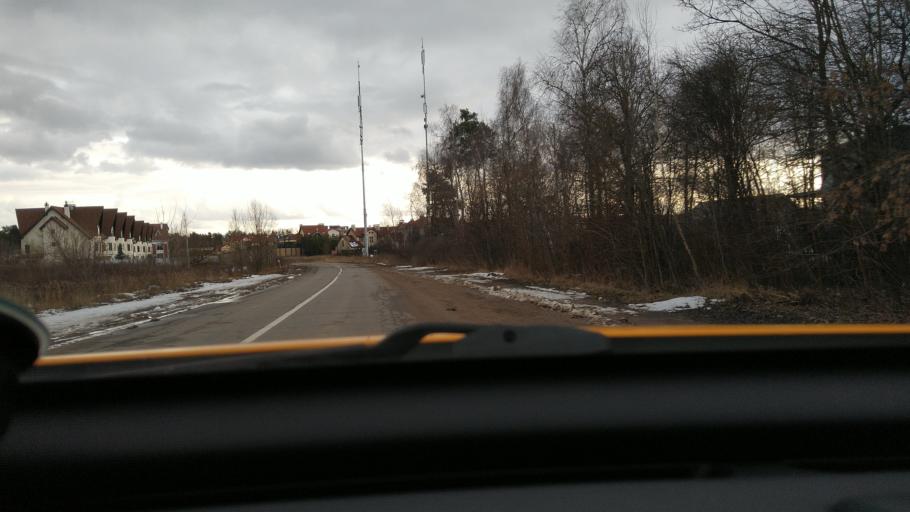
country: RU
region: Moskovskaya
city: Petrovo-Dal'neye
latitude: 55.7538
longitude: 37.1996
